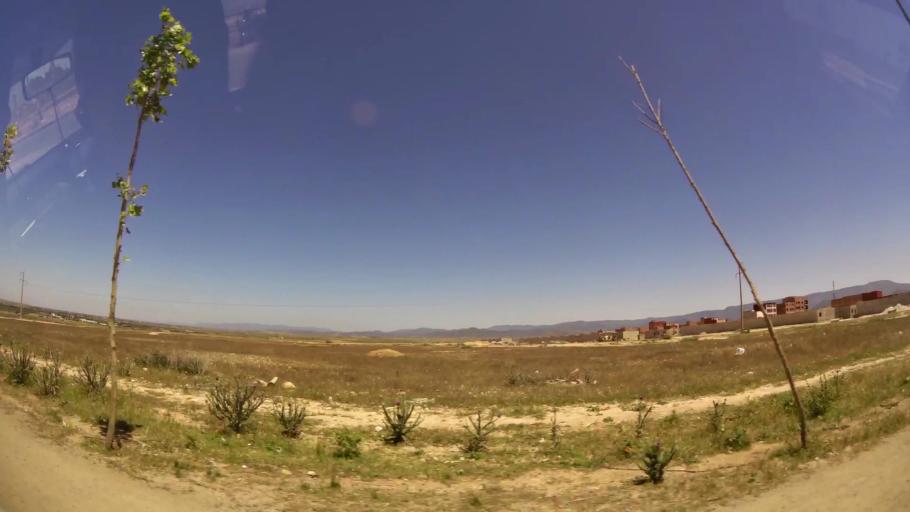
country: MA
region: Oriental
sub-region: Oujda-Angad
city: Oujda
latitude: 34.6841
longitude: -1.8581
